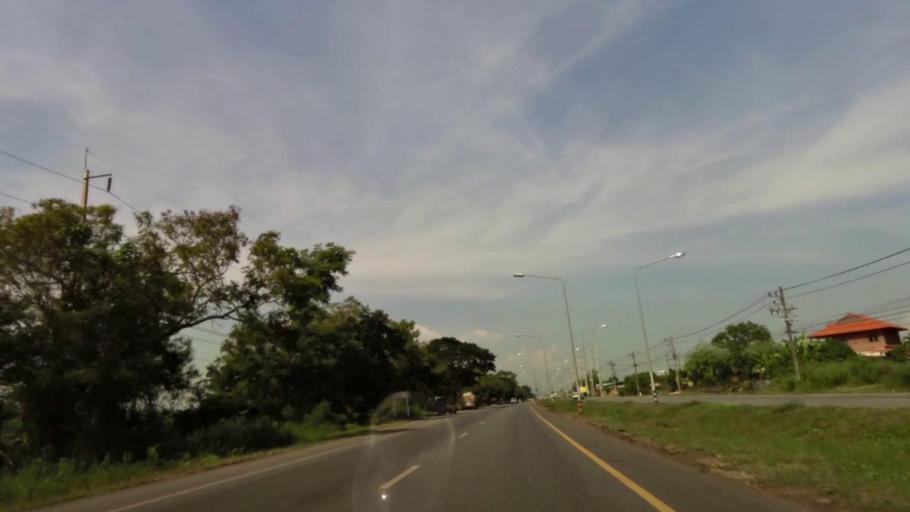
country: TH
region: Uttaradit
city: Uttaradit
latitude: 17.5635
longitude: 100.1596
